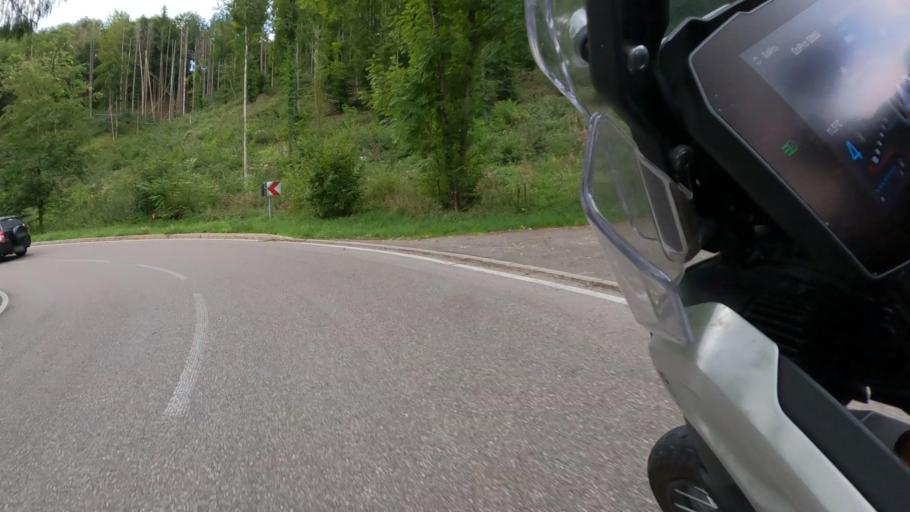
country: DE
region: Baden-Wuerttemberg
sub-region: Freiburg Region
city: Eggingen
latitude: 47.7000
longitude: 8.3740
